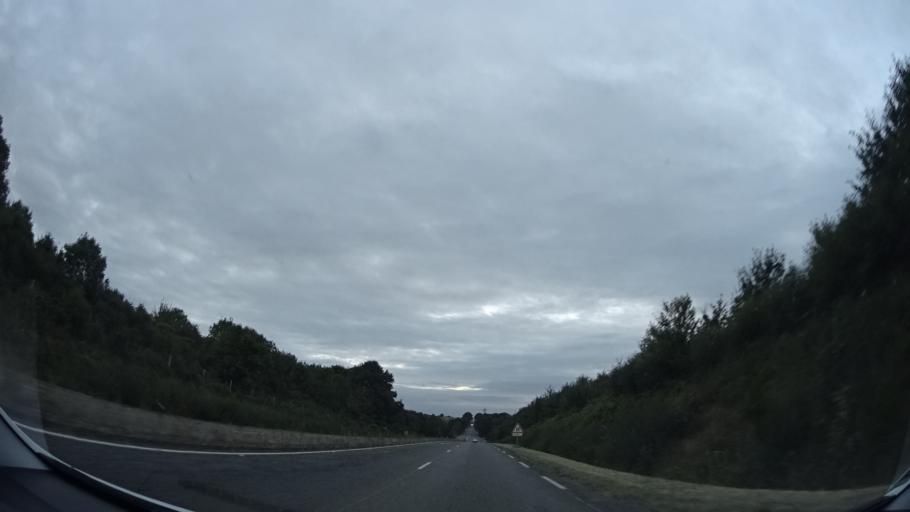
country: FR
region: Pays de la Loire
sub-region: Departement de la Mayenne
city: Vaiges
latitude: 48.0377
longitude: -0.4369
